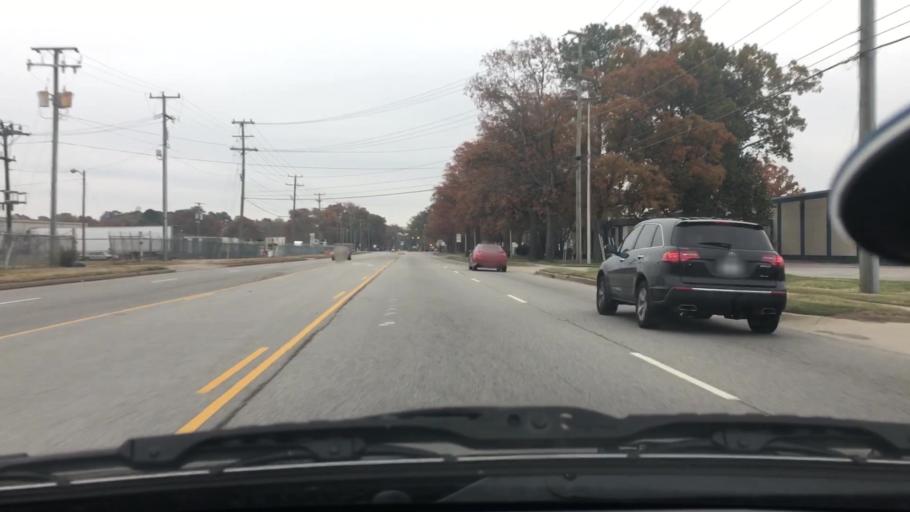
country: US
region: Virginia
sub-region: City of Norfolk
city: Norfolk
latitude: 36.8578
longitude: -76.2417
